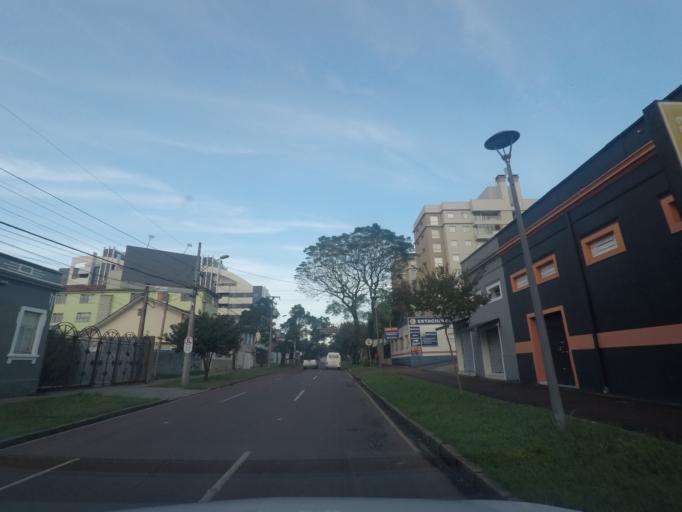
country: BR
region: Parana
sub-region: Curitiba
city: Curitiba
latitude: -25.4448
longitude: -49.2673
